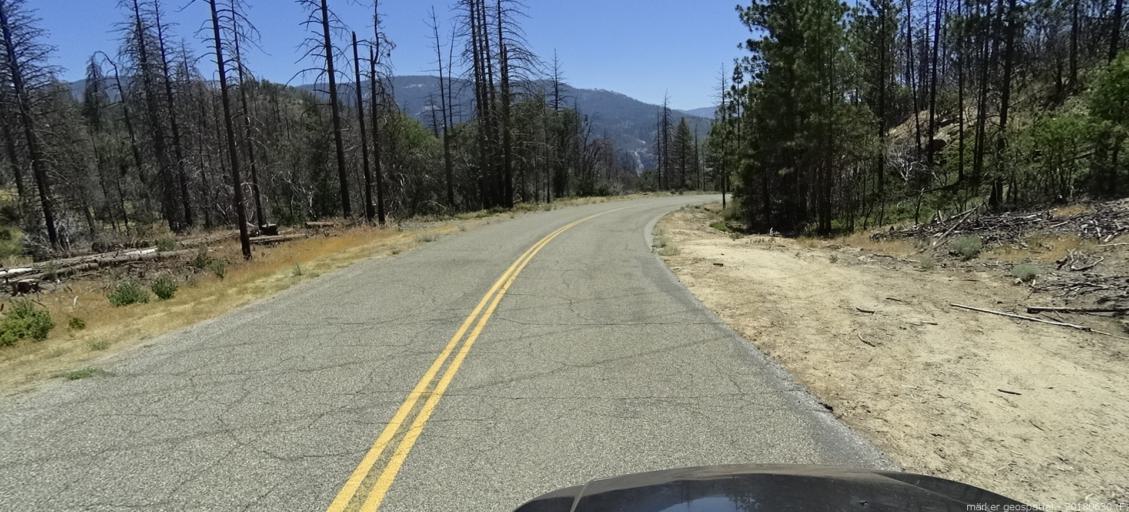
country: US
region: California
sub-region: Fresno County
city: Auberry
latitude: 37.2504
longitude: -119.3478
